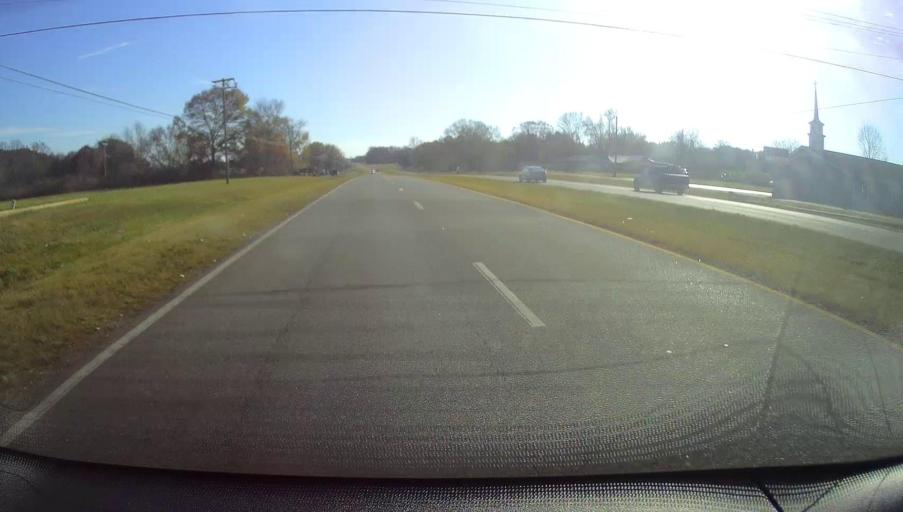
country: US
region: Alabama
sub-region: Limestone County
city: Athens
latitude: 34.7287
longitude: -86.9570
